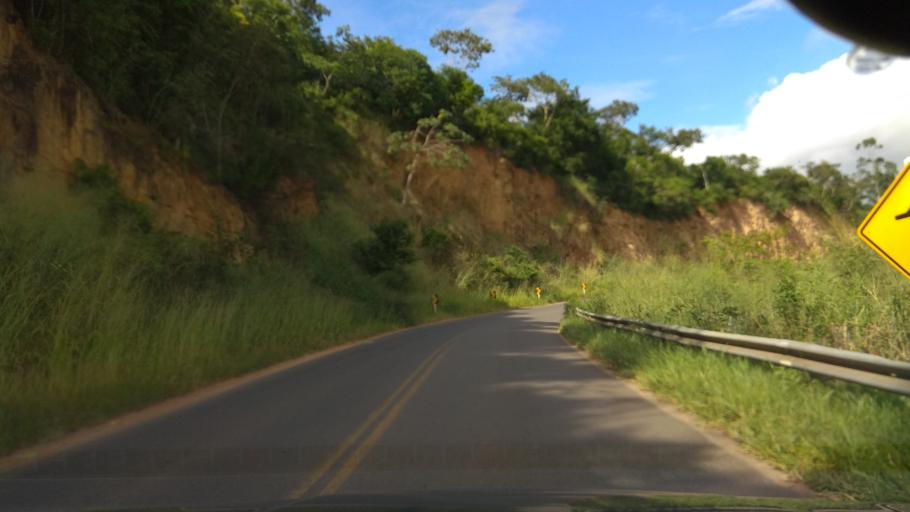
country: BR
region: Bahia
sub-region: Ubaira
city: Ubaira
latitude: -13.2574
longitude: -39.6632
